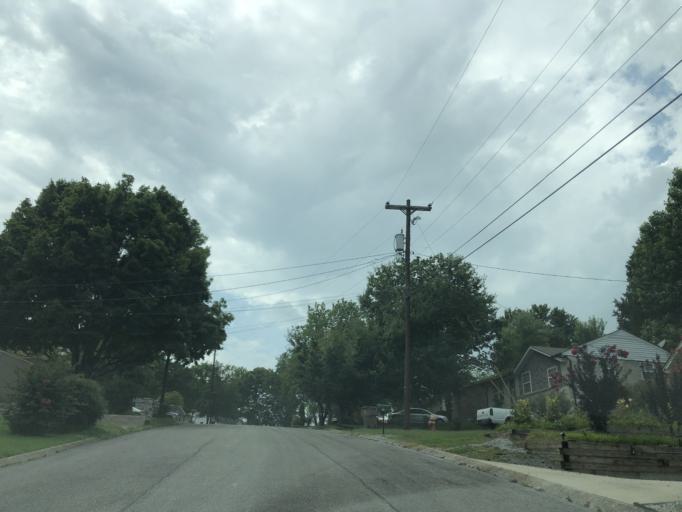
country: US
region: Tennessee
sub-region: Williamson County
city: Nolensville
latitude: 36.0558
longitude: -86.6788
